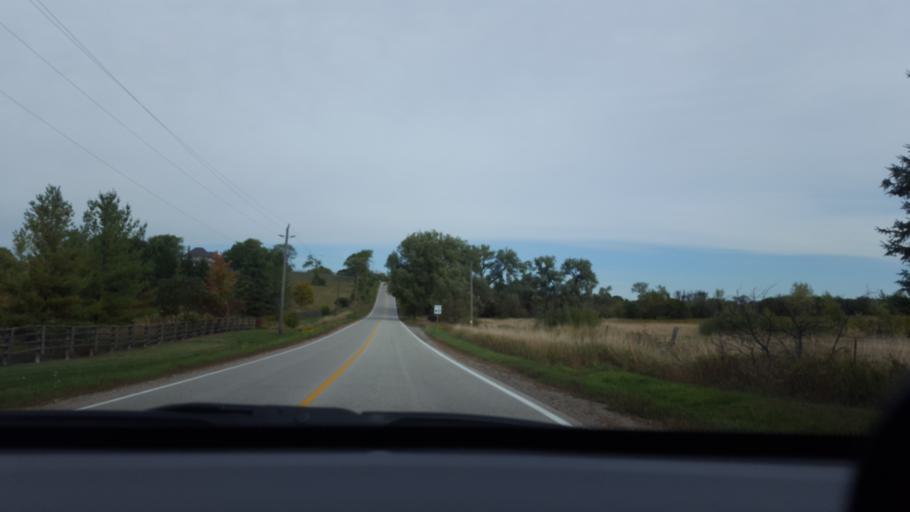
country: CA
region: Ontario
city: Newmarket
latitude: 44.0072
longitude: -79.5489
